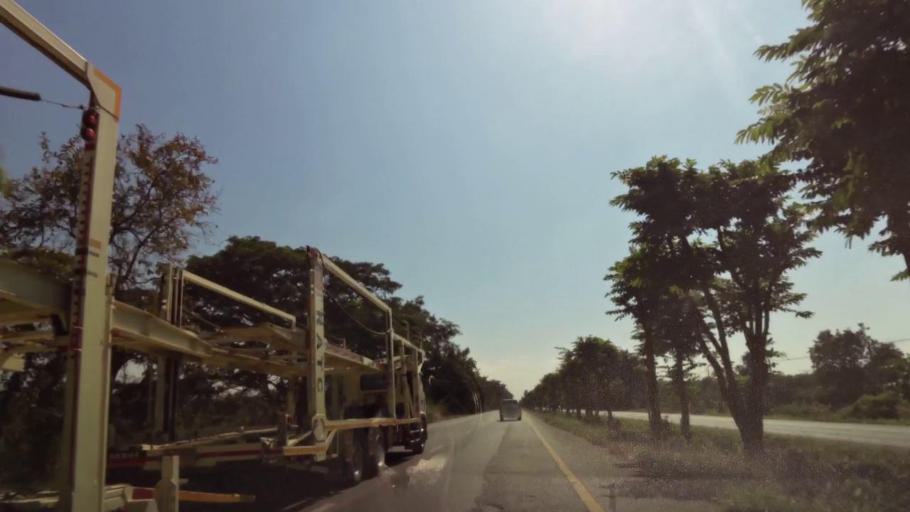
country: TH
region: Nakhon Sawan
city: Kao Liao
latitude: 15.7924
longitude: 100.1207
